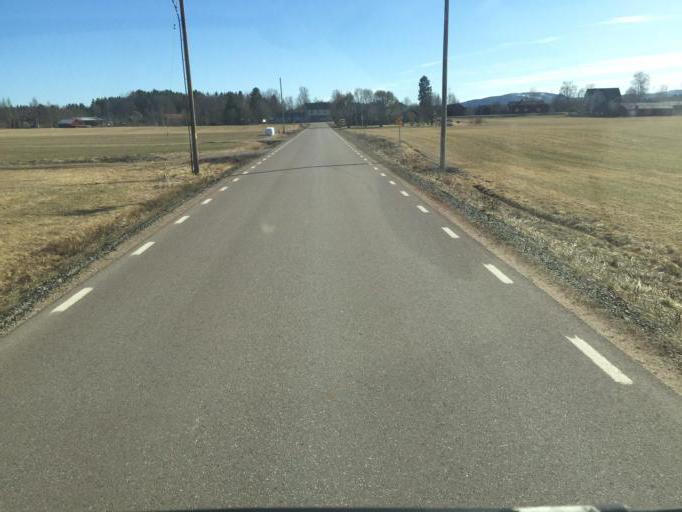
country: SE
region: Dalarna
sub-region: Vansbro Kommun
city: Vansbro
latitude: 60.4617
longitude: 13.9997
